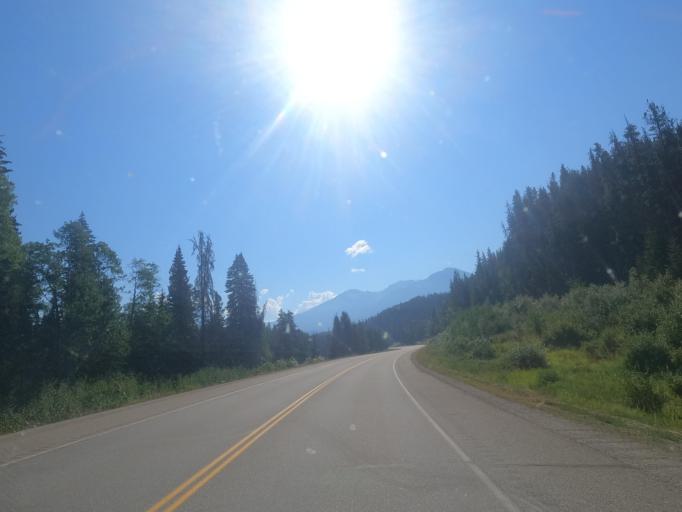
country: CA
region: Alberta
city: Jasper Park Lodge
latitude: 52.8616
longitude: -118.6419
